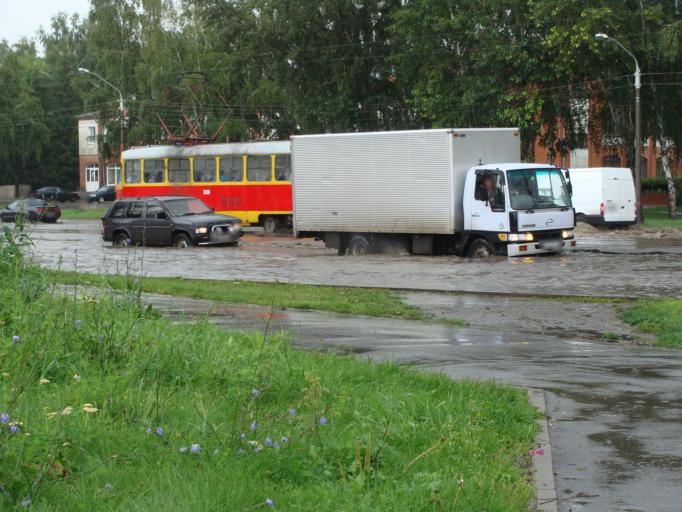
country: RU
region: Altai Krai
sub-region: Gorod Barnaulskiy
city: Barnaul
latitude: 53.3602
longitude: 83.6915
